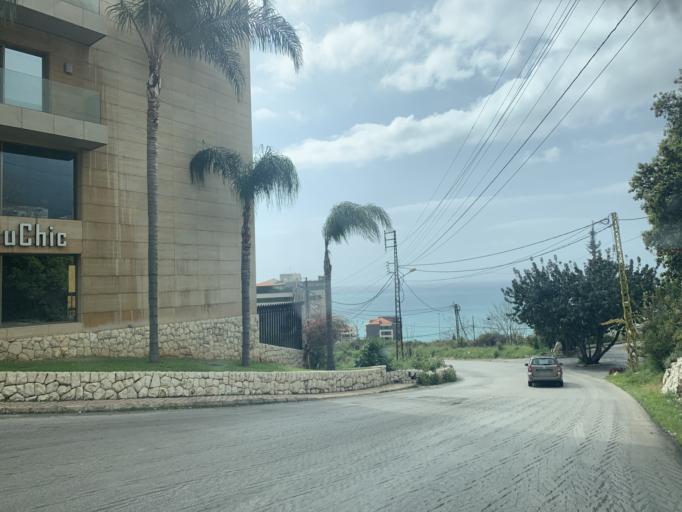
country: LB
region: Mont-Liban
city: Djounie
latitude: 34.0040
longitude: 35.6501
